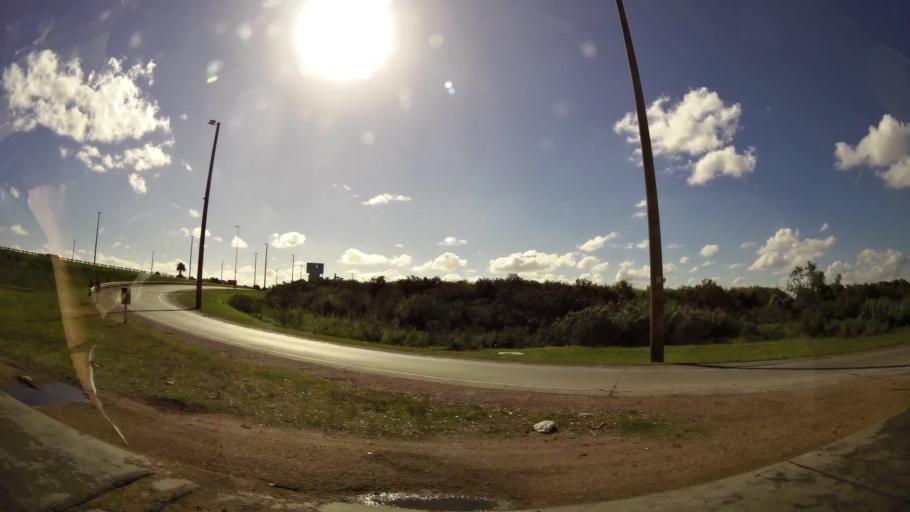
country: UY
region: Montevideo
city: Montevideo
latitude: -34.8560
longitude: -56.2561
